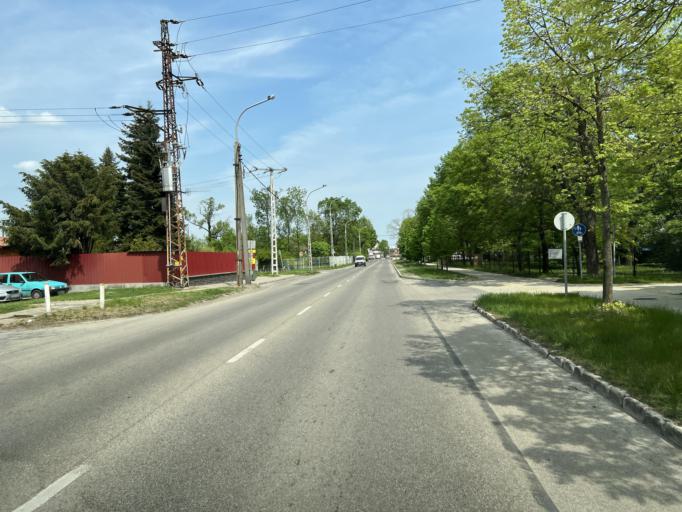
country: HU
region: Pest
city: Nagykoros
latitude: 47.0423
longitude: 19.7844
